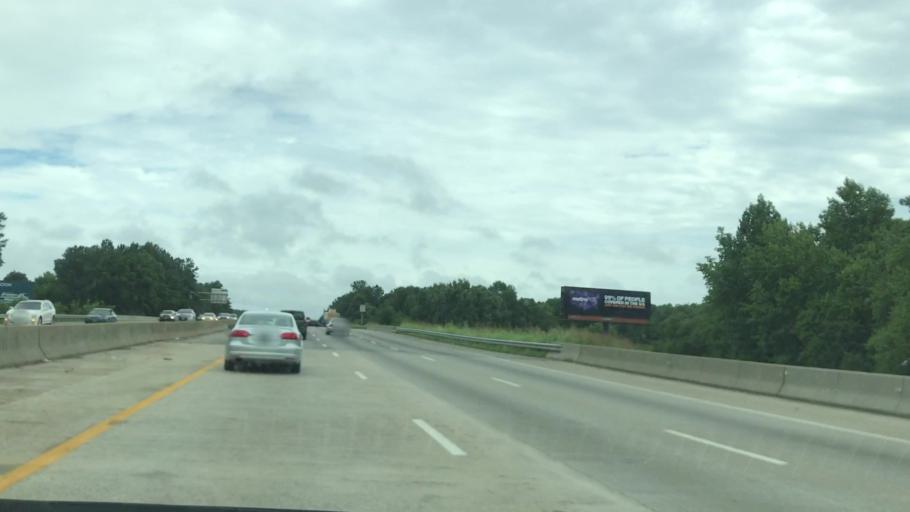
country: US
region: Virginia
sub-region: Chesterfield County
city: Bellwood
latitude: 37.4085
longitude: -77.4259
